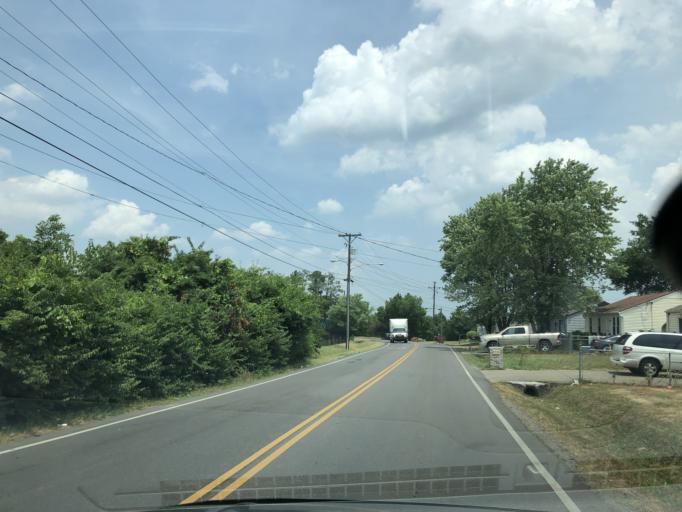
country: US
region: Tennessee
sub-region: Davidson County
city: Oak Hill
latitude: 36.0644
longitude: -86.6870
